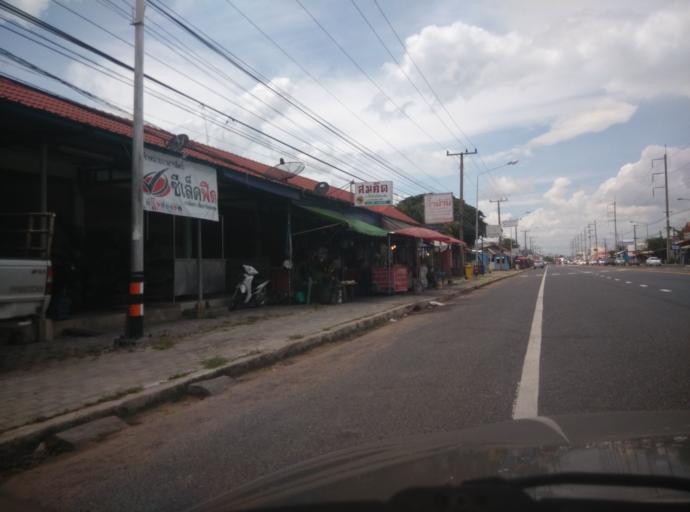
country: TH
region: Sisaket
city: Huai Thap Than
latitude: 15.0508
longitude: 104.0261
